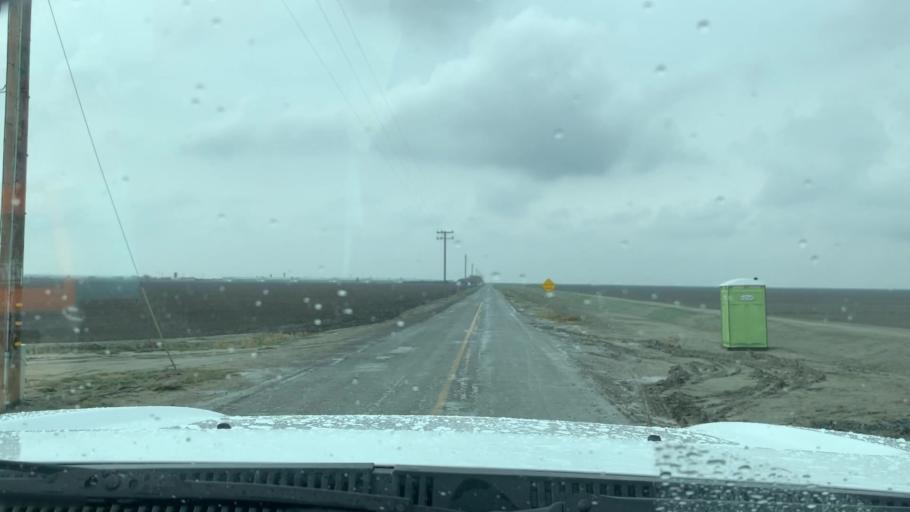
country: US
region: California
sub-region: Kings County
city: Corcoran
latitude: 36.0072
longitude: -119.5365
